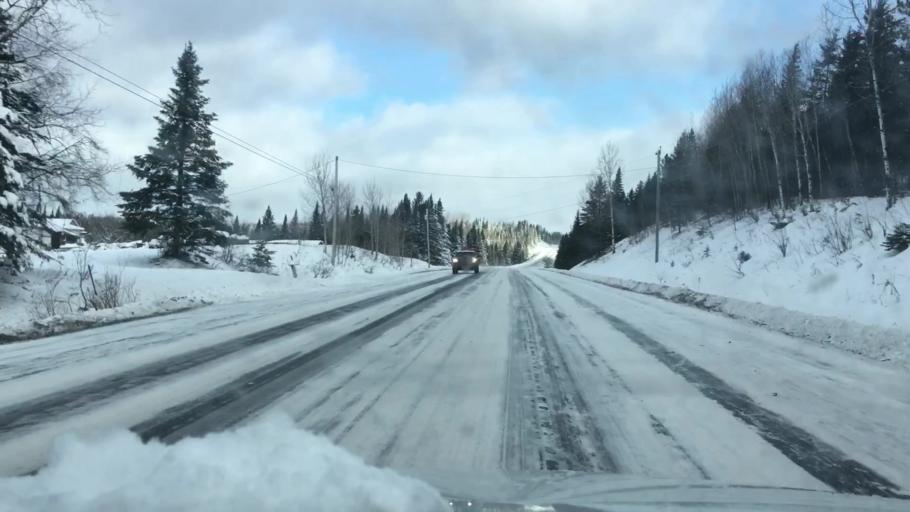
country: US
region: Maine
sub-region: Aroostook County
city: Van Buren
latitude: 47.0365
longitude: -68.0050
